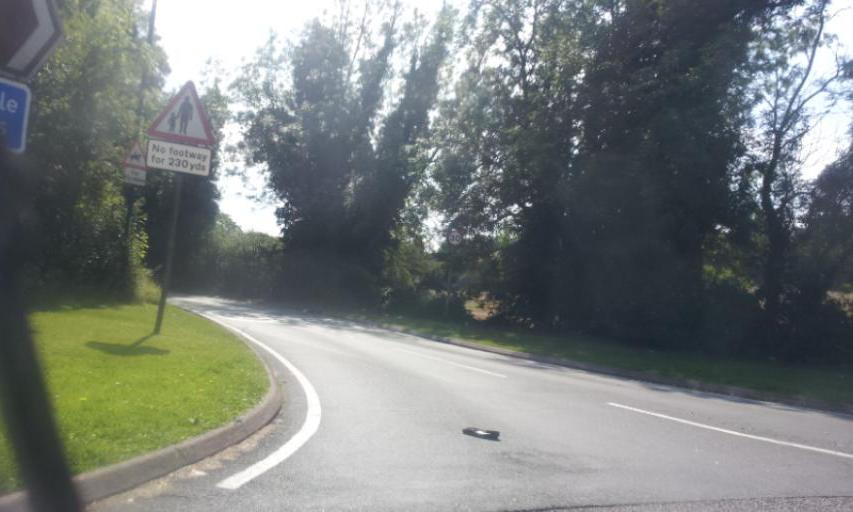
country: GB
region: England
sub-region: Kent
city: Gillingham
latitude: 51.3627
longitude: 0.5550
